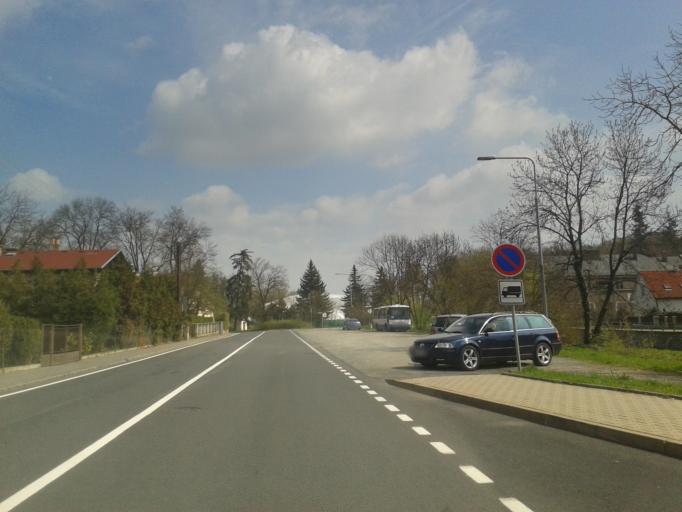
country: CZ
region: Central Bohemia
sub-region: Okres Beroun
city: Horovice
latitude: 49.8393
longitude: 13.9011
